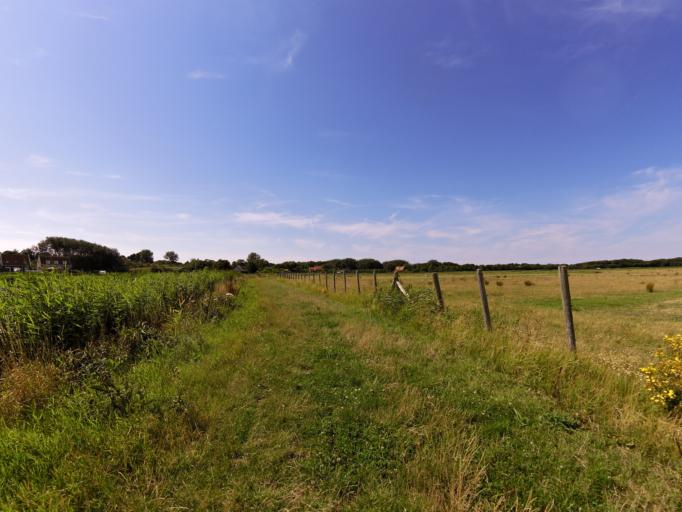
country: NL
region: South Holland
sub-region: Gemeente Goeree-Overflakkee
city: Ouddorp
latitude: 51.8007
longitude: 3.8708
